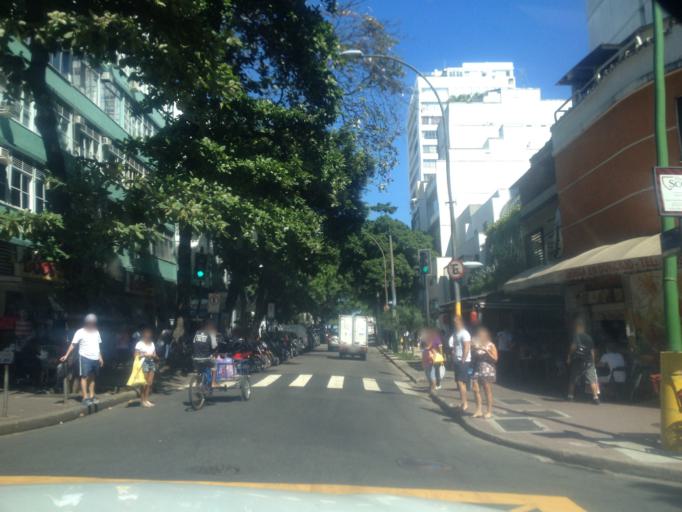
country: BR
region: Rio de Janeiro
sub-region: Rio De Janeiro
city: Rio de Janeiro
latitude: -22.9838
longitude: -43.2092
